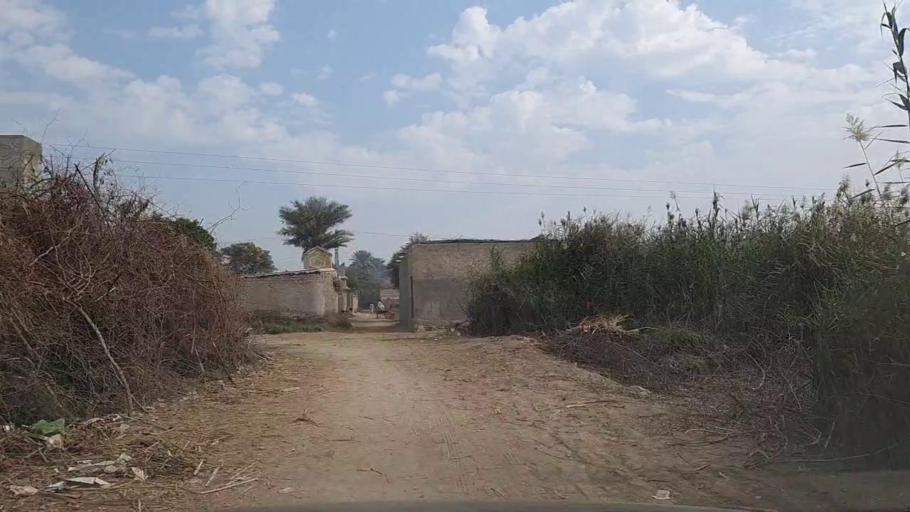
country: PK
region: Sindh
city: Daur
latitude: 26.3984
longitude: 68.3554
